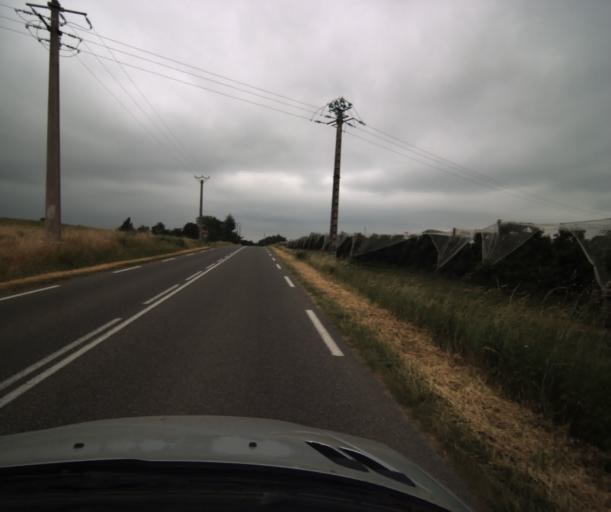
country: FR
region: Midi-Pyrenees
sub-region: Departement du Tarn-et-Garonne
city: Saint-Nicolas-de-la-Grave
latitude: 44.0336
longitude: 1.0382
